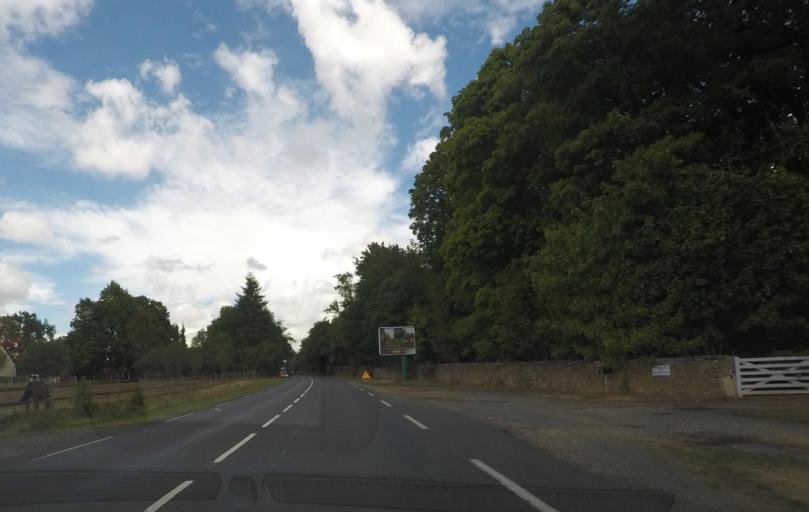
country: FR
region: Pays de la Loire
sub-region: Departement de la Sarthe
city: Champagne
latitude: 48.0657
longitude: 0.2899
